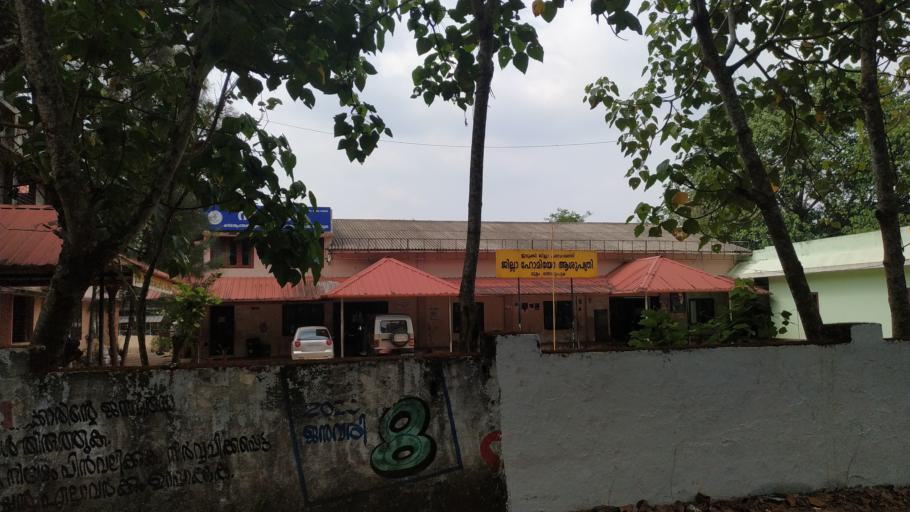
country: IN
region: Kerala
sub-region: Kottayam
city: Lalam
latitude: 9.8440
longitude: 76.7394
